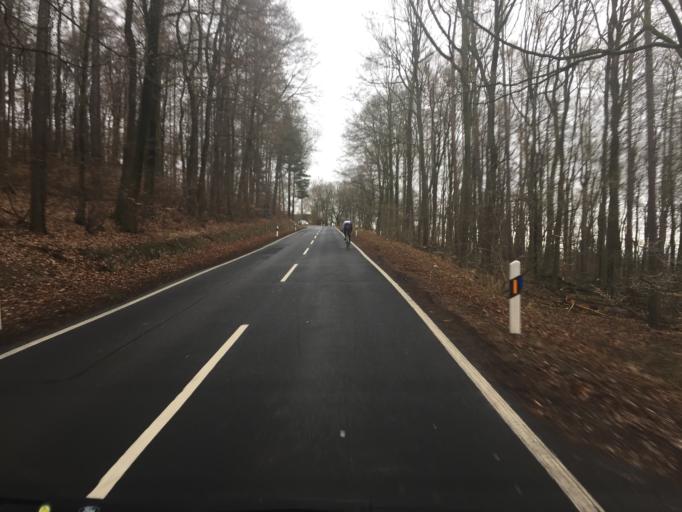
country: DE
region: Bavaria
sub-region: Regierungsbezirk Unterfranken
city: Alzenau in Unterfranken
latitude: 50.0492
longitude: 9.0809
